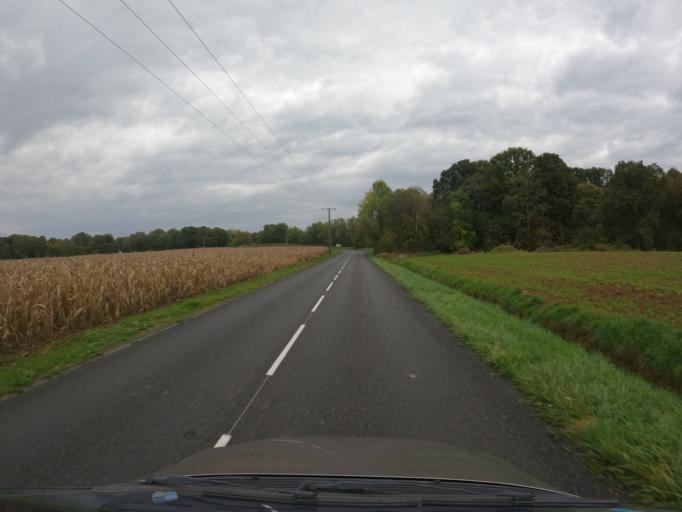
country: FR
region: Ile-de-France
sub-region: Departement de Seine-et-Marne
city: Serris
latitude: 48.8268
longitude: 2.7621
